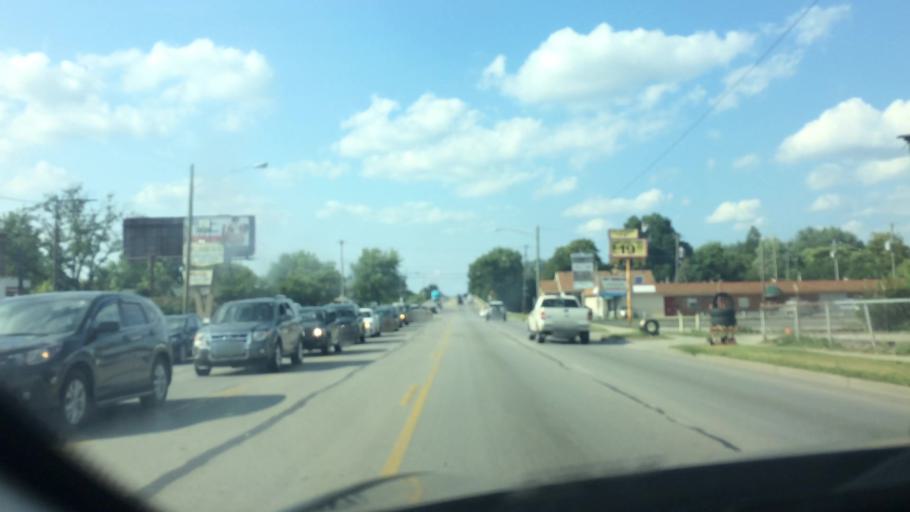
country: US
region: Ohio
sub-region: Lucas County
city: Ottawa Hills
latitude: 41.6261
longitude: -83.6258
